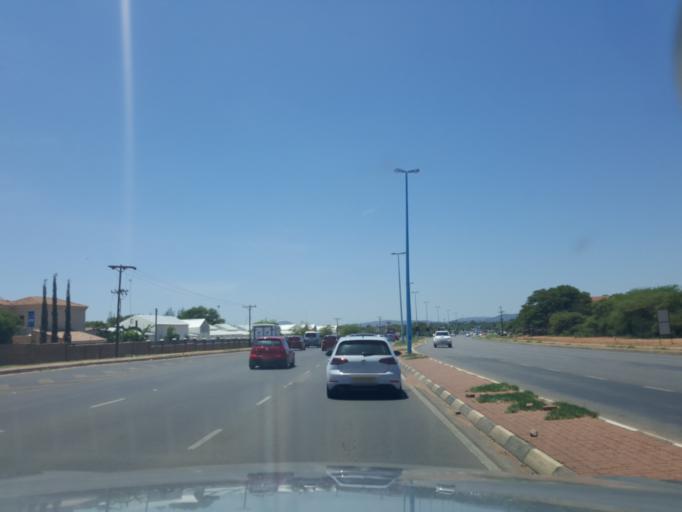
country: BW
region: Kweneng
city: Mogoditshane
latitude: -24.6360
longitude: 25.8779
